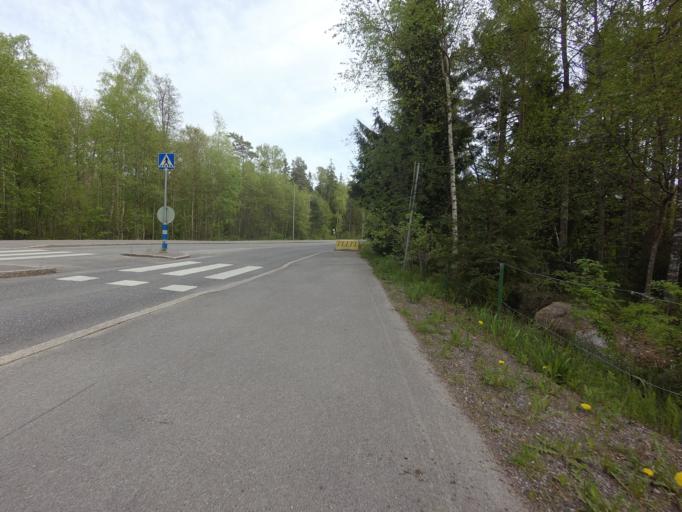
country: FI
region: Uusimaa
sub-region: Helsinki
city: Koukkuniemi
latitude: 60.1247
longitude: 24.7135
